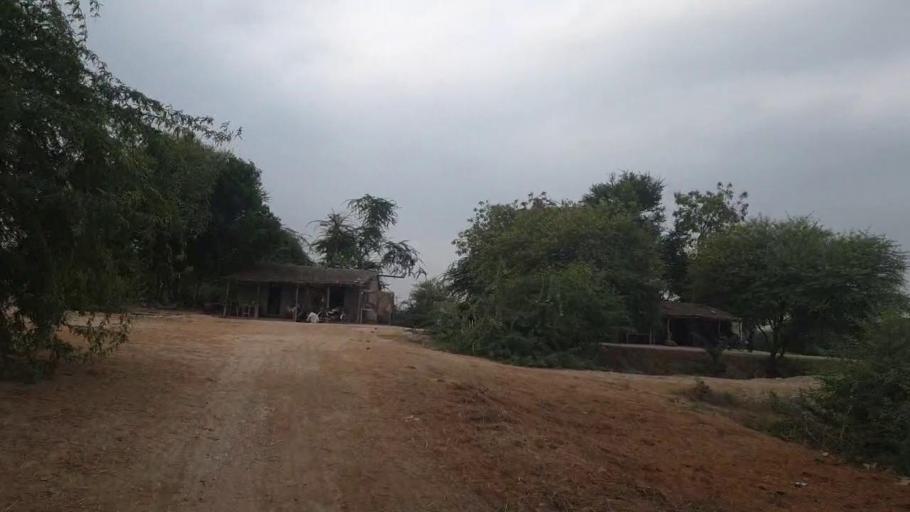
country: PK
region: Sindh
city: Badin
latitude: 24.6165
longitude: 68.6809
